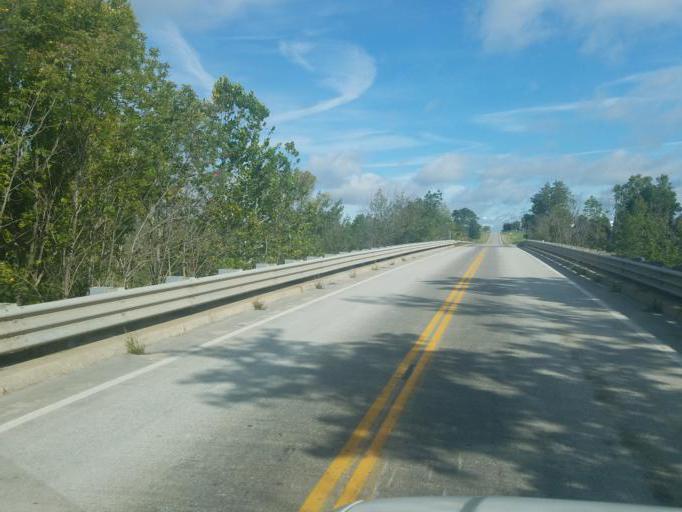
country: US
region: Ohio
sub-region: Wayne County
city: West Salem
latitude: 41.0384
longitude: -82.1260
